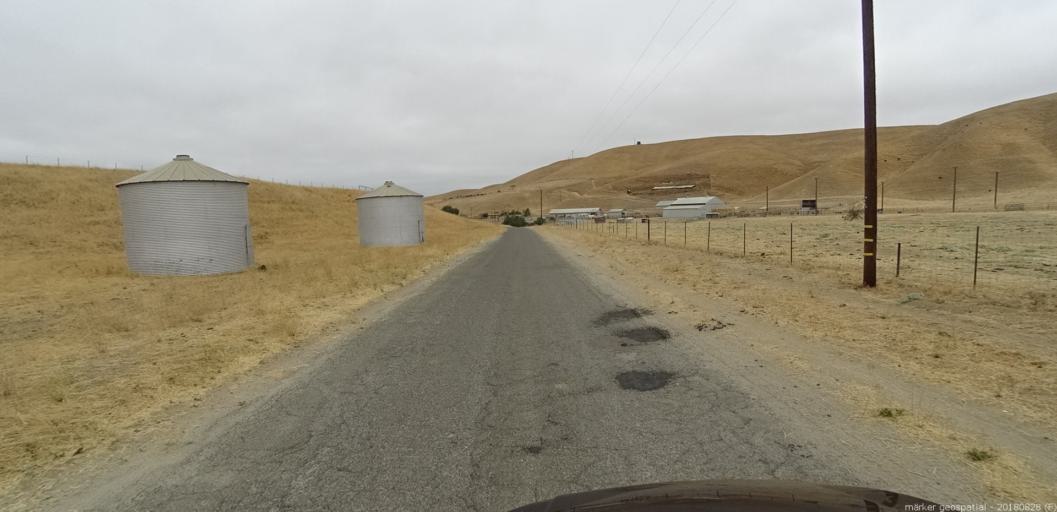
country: US
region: California
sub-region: San Luis Obispo County
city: Lake Nacimiento
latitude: 35.9612
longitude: -120.8339
